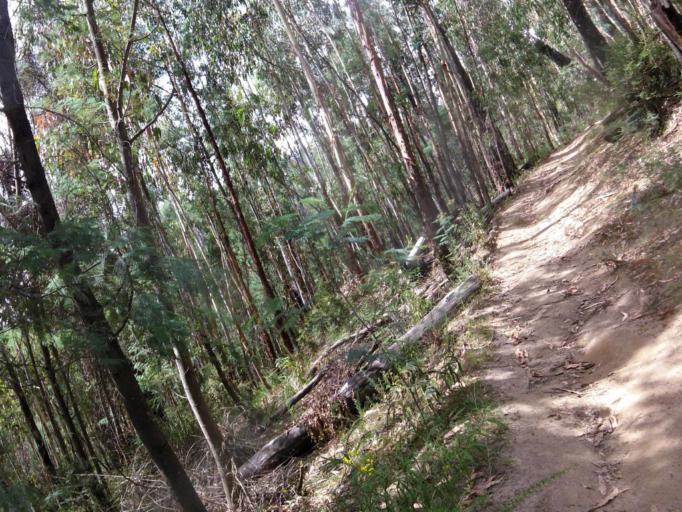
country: AU
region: Victoria
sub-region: Murrindindi
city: Alexandra
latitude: -37.4037
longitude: 145.5707
